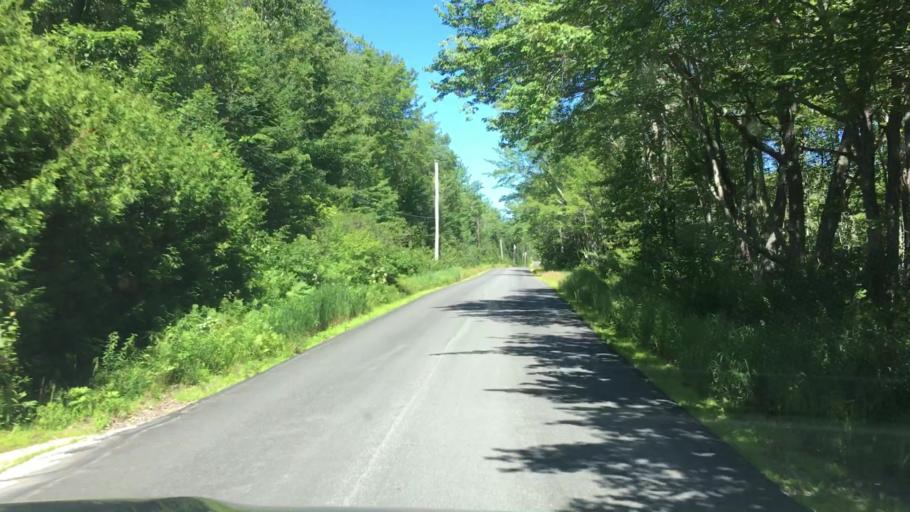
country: US
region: Maine
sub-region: Hancock County
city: Sedgwick
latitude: 44.3161
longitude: -68.6196
